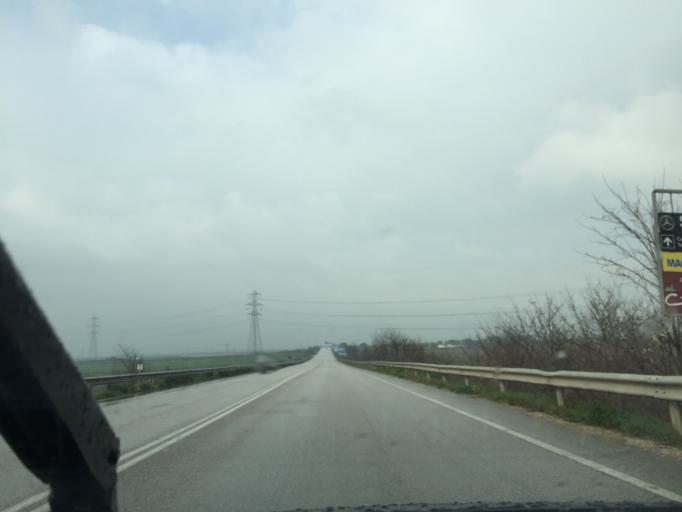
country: IT
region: Apulia
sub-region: Provincia di Foggia
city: Foggia
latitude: 41.4981
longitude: 15.5308
